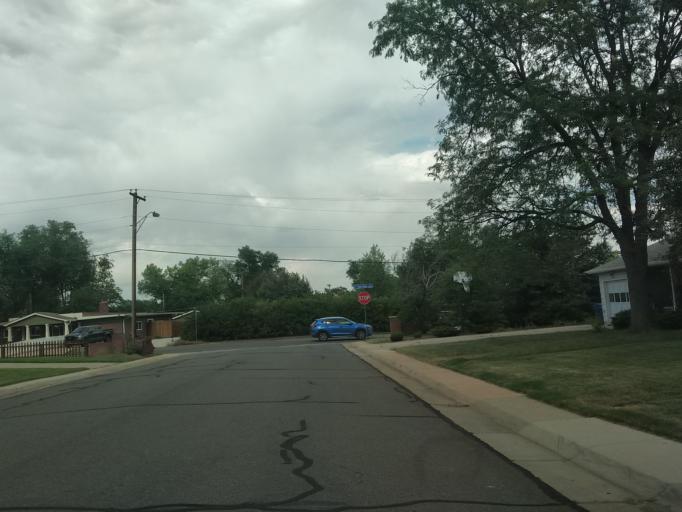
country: US
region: Colorado
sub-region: Jefferson County
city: Lakewood
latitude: 39.6993
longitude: -105.1009
